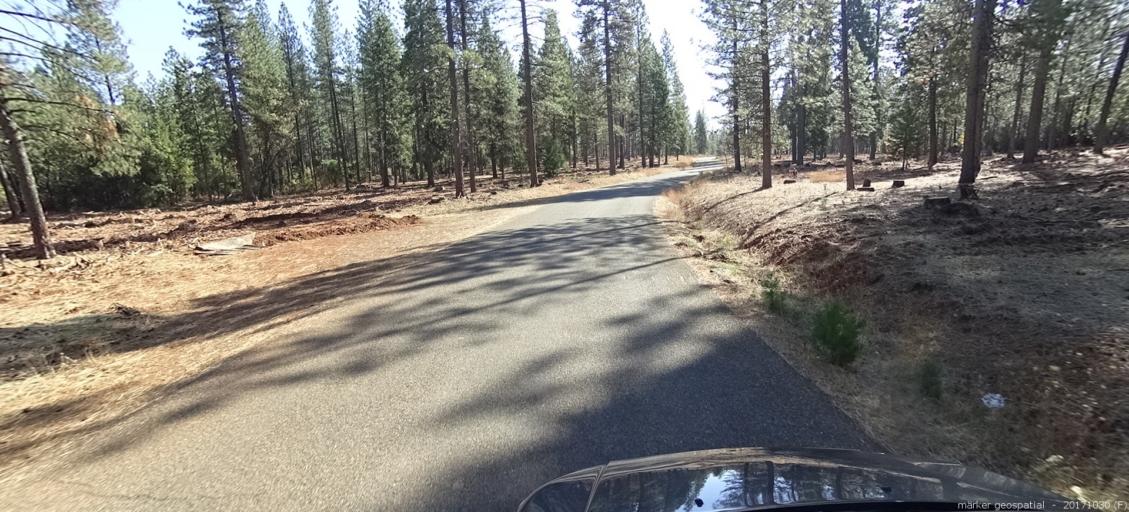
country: US
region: California
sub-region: Shasta County
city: Shingletown
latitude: 40.6175
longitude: -121.8874
